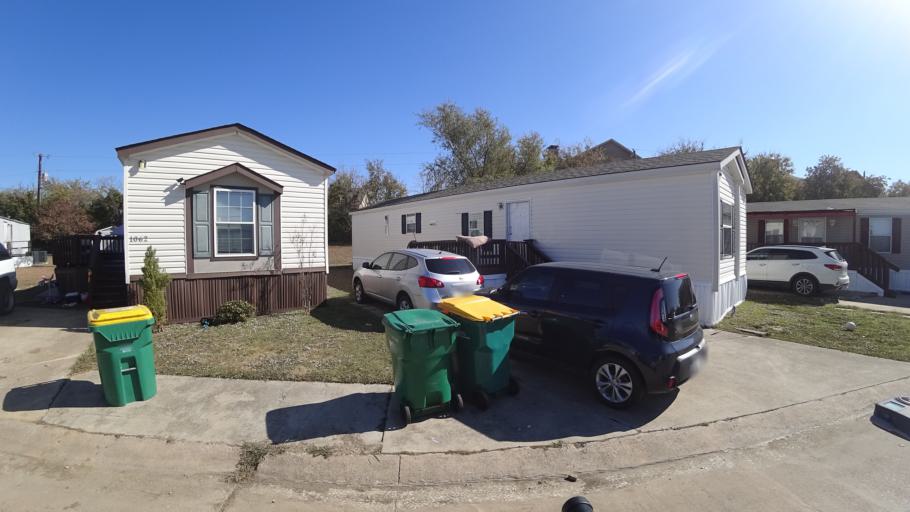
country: US
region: Texas
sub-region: Denton County
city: Lewisville
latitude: 33.0406
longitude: -96.9320
